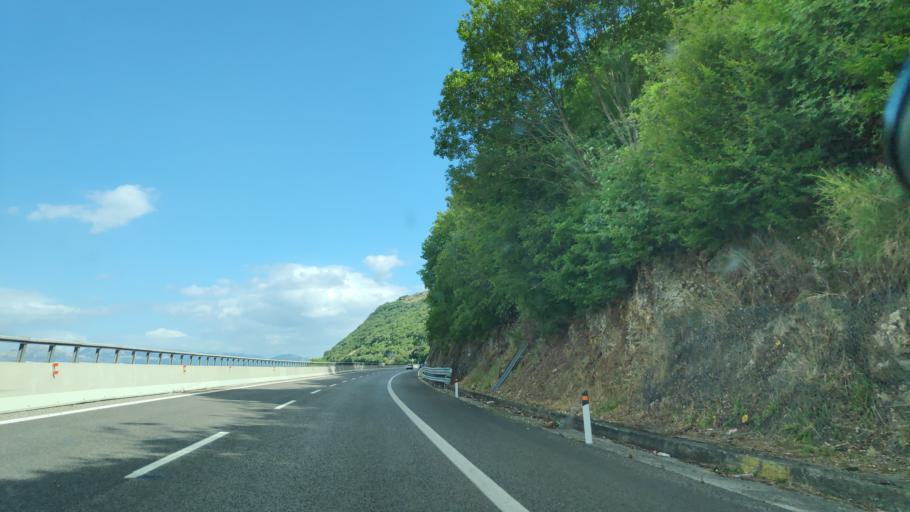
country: IT
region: Campania
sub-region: Provincia di Salerno
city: Sicignano degli Alburni
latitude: 40.5961
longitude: 15.3207
